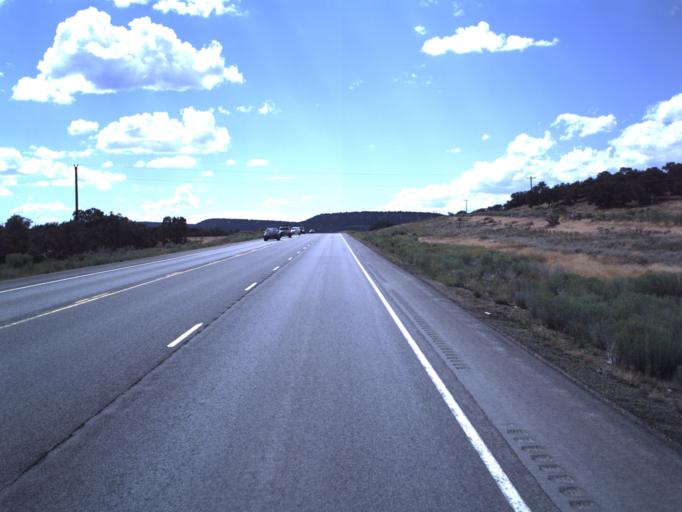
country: US
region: Utah
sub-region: Duchesne County
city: Duchesne
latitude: 40.1716
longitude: -110.5750
